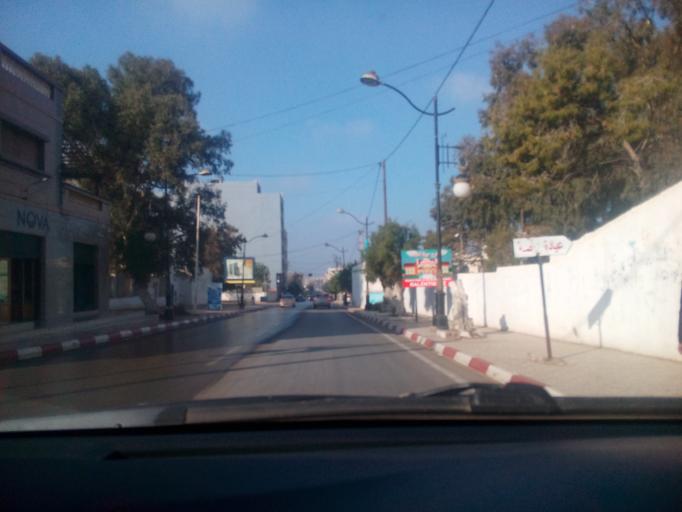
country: DZ
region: Oran
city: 'Ain el Turk
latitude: 35.7363
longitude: -0.7446
